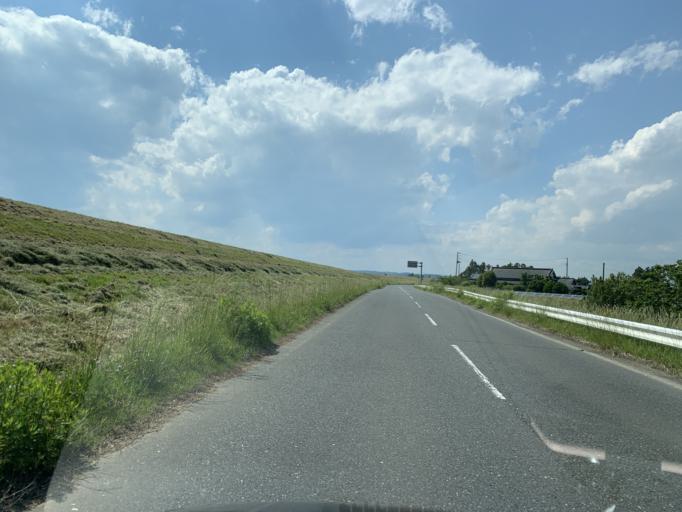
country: JP
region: Miyagi
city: Matsushima
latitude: 38.4442
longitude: 141.1134
